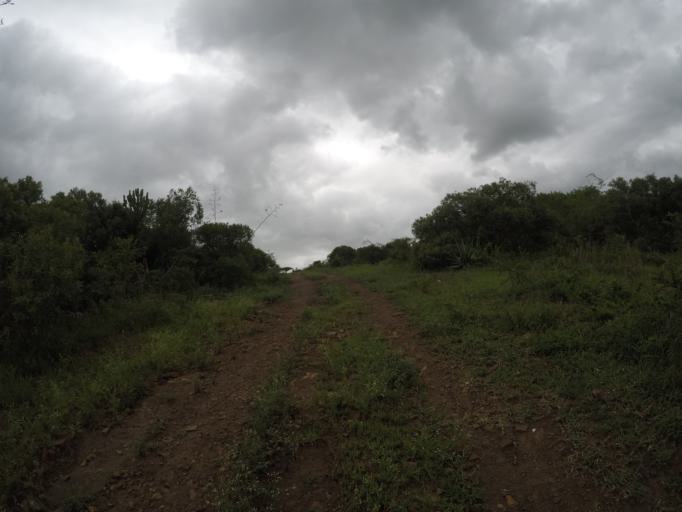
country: ZA
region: KwaZulu-Natal
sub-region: uThungulu District Municipality
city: Empangeni
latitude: -28.5781
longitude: 31.8700
